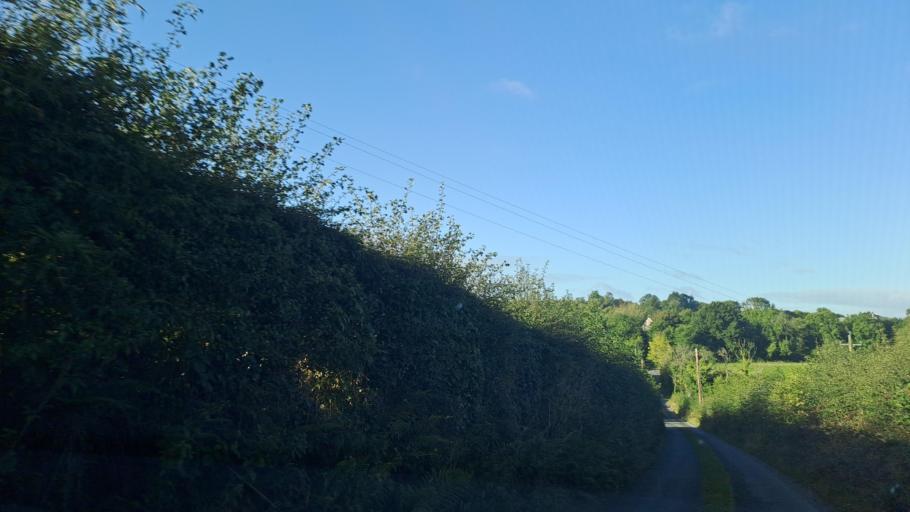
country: IE
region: Ulster
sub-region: An Cabhan
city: Kingscourt
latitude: 53.9894
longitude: -6.8721
